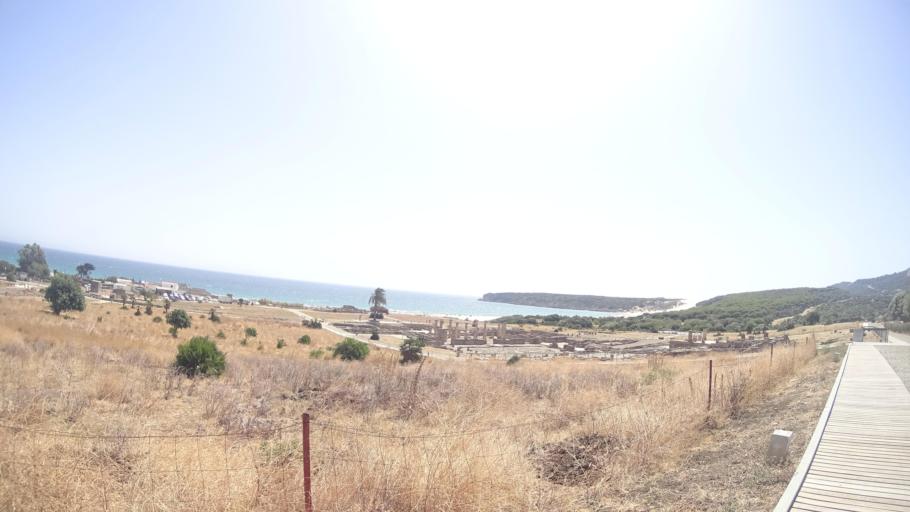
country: ES
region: Andalusia
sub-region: Provincia de Cadiz
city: Zahara de los Atunes
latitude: 36.0902
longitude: -5.7738
